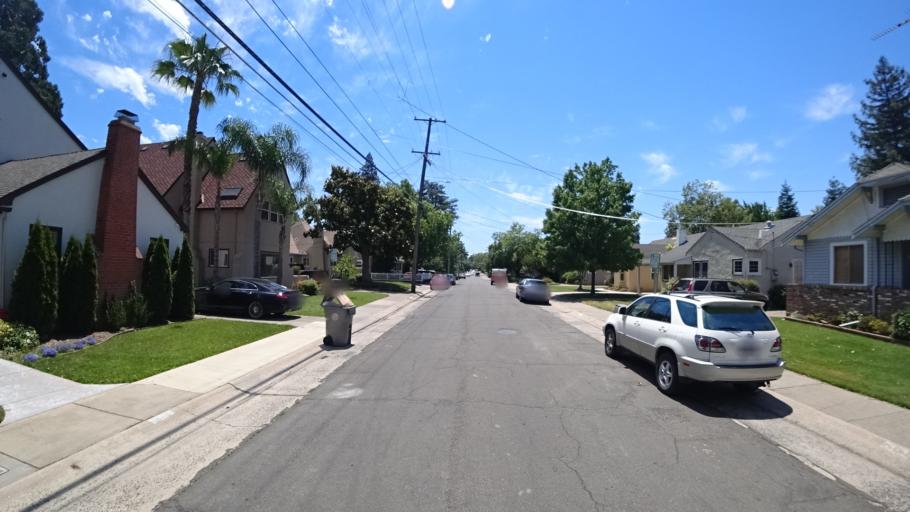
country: US
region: California
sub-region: Sacramento County
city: Sacramento
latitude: 38.5680
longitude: -121.4411
